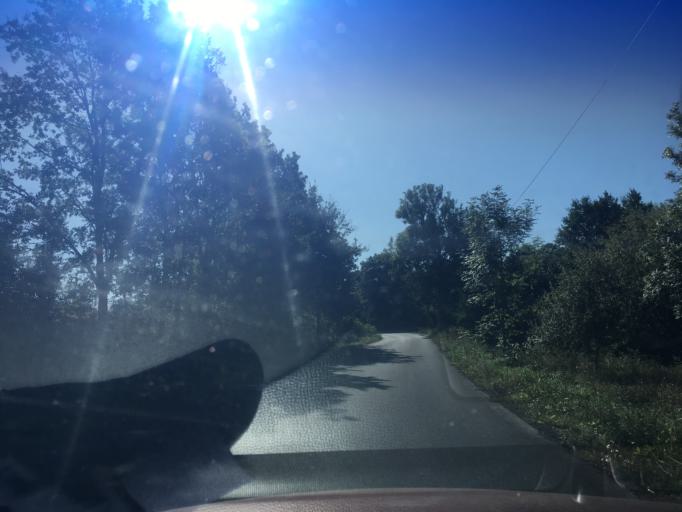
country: PL
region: Lower Silesian Voivodeship
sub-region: Powiat lubanski
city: Lesna
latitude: 51.0329
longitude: 15.1789
